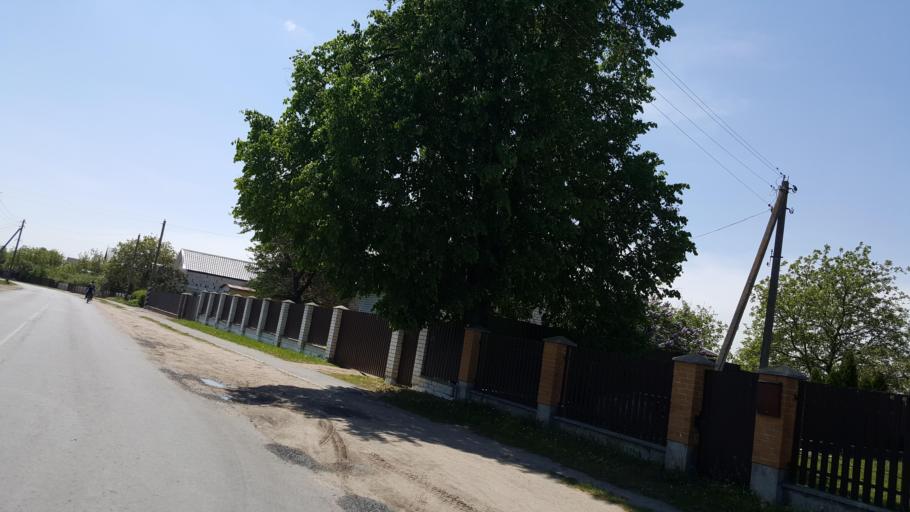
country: BY
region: Brest
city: Charnawchytsy
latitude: 52.2189
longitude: 23.7427
